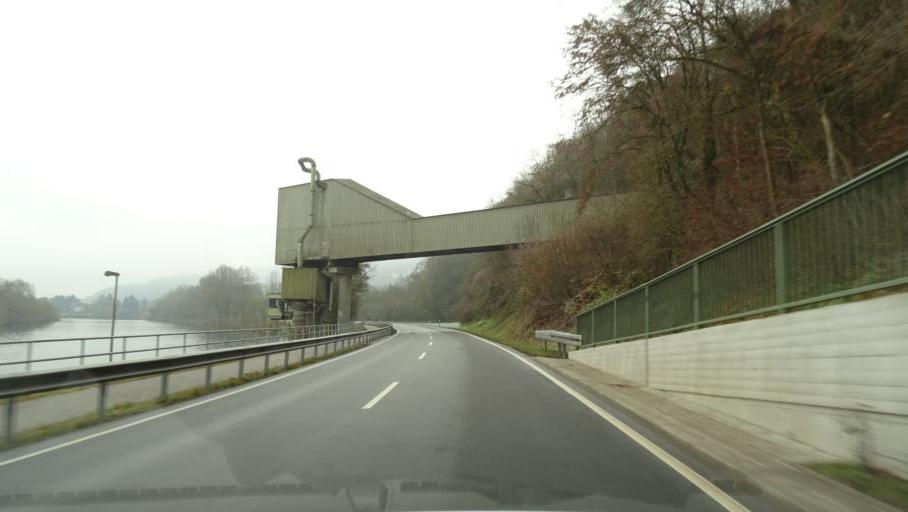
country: DE
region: Baden-Wuerttemberg
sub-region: Karlsruhe Region
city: Hassmersheim
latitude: 49.2910
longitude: 9.1296
